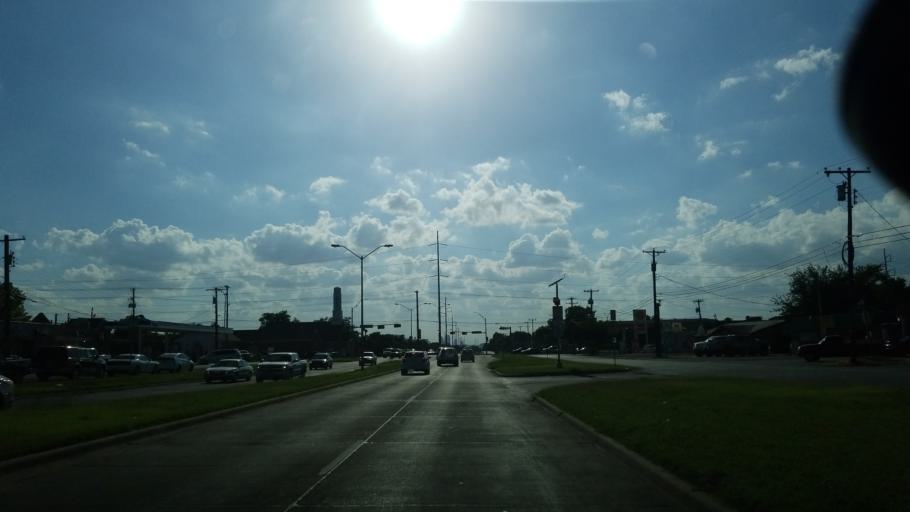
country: US
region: Texas
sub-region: Dallas County
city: Balch Springs
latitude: 32.7724
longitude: -96.6984
